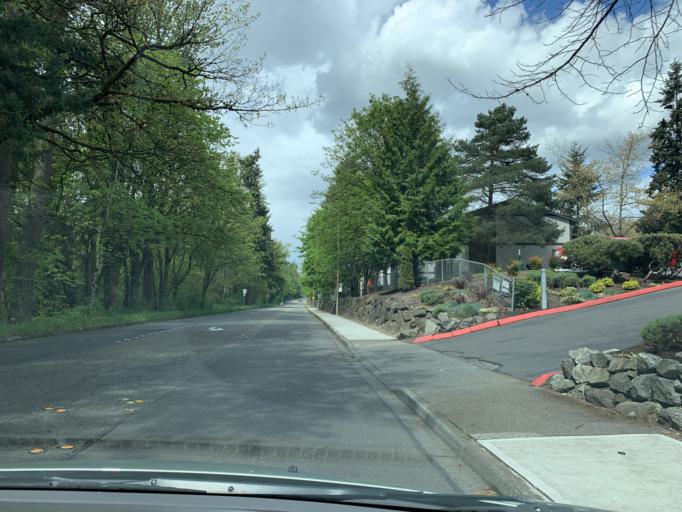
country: US
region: Washington
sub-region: King County
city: Kent
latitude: 47.3699
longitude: -122.2080
